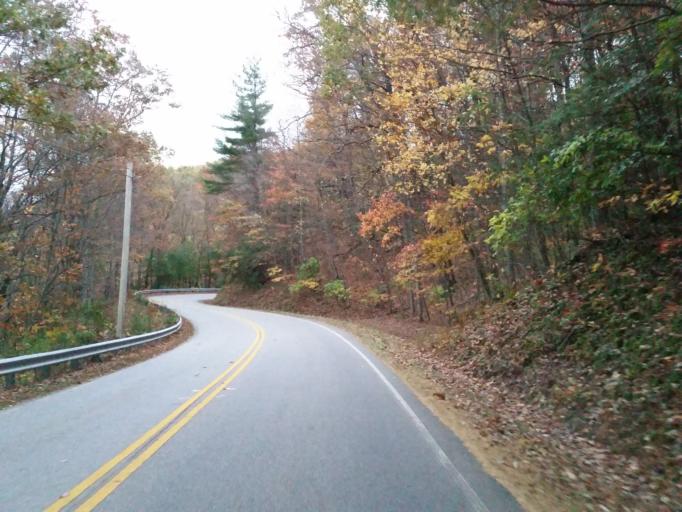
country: US
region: Georgia
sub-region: Lumpkin County
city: Dahlonega
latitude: 34.7041
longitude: -84.0404
